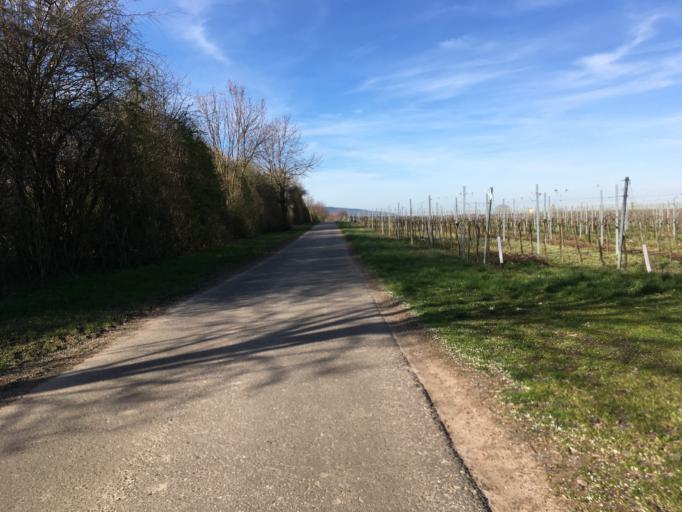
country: DE
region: Rheinland-Pfalz
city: Kirrweiler
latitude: 49.3240
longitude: 8.1589
